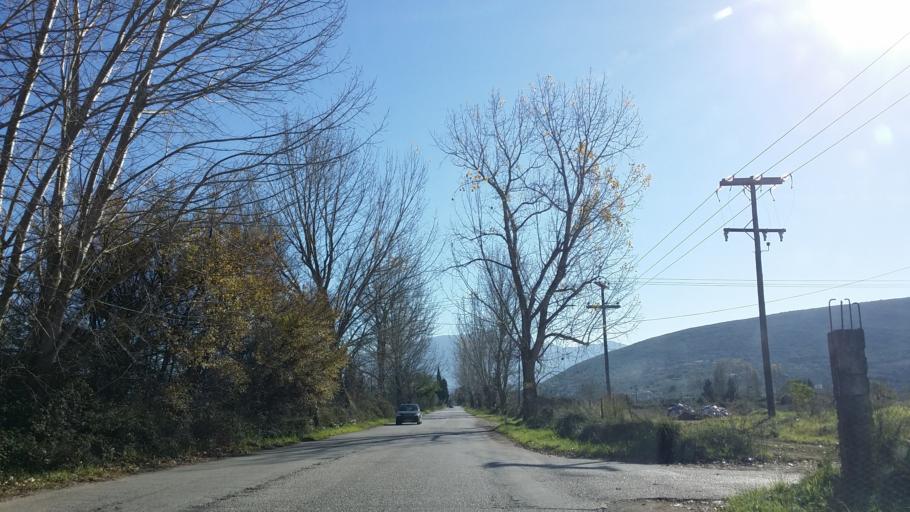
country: GR
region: West Greece
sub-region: Nomos Aitolias kai Akarnanias
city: Vonitsa
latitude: 38.9150
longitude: 20.8815
